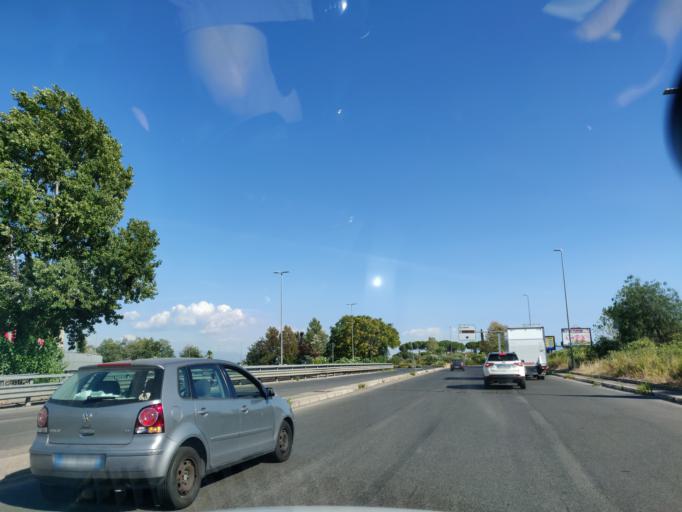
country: IT
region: Latium
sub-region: Citta metropolitana di Roma Capitale
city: Colle Verde
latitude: 41.9694
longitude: 12.5380
